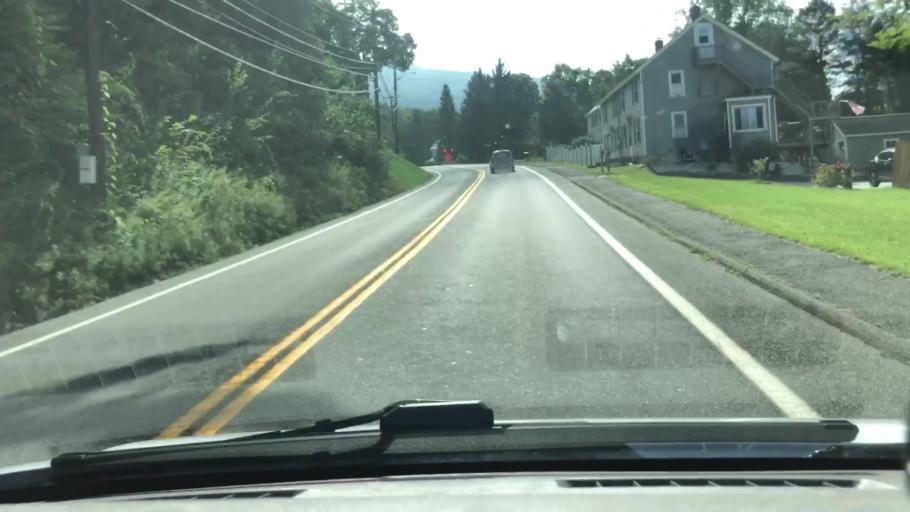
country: US
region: Massachusetts
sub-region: Berkshire County
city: North Adams
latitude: 42.6967
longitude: -73.0903
